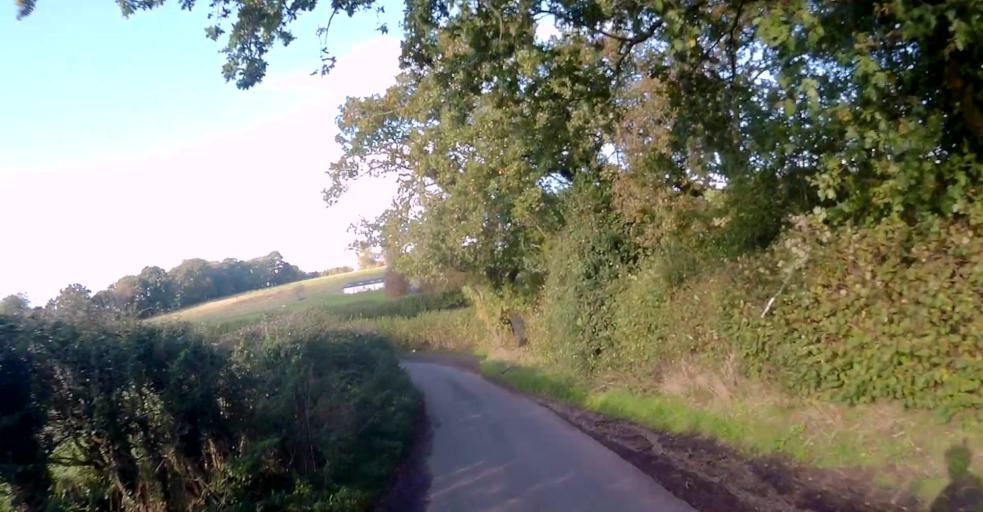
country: GB
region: England
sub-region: Surrey
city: Farnham
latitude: 51.2115
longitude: -0.8556
